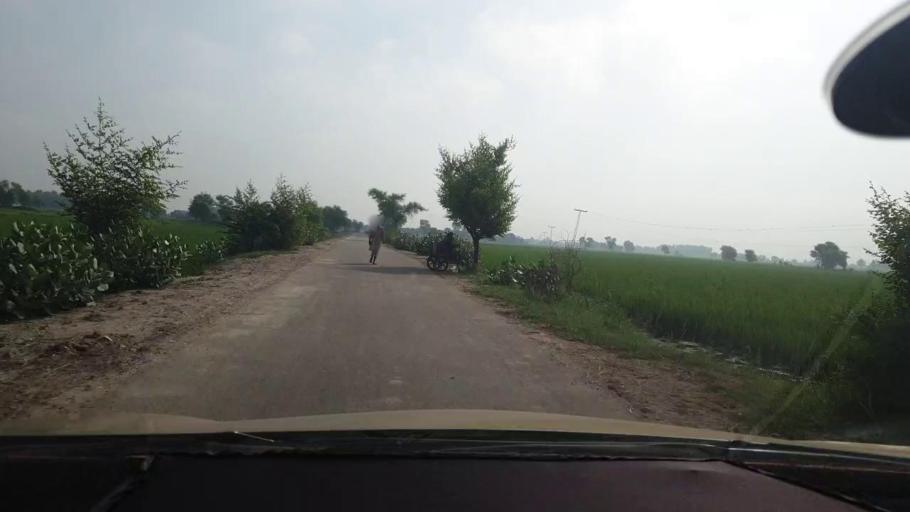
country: PK
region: Sindh
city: Goth Garelo
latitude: 27.4822
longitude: 68.0212
